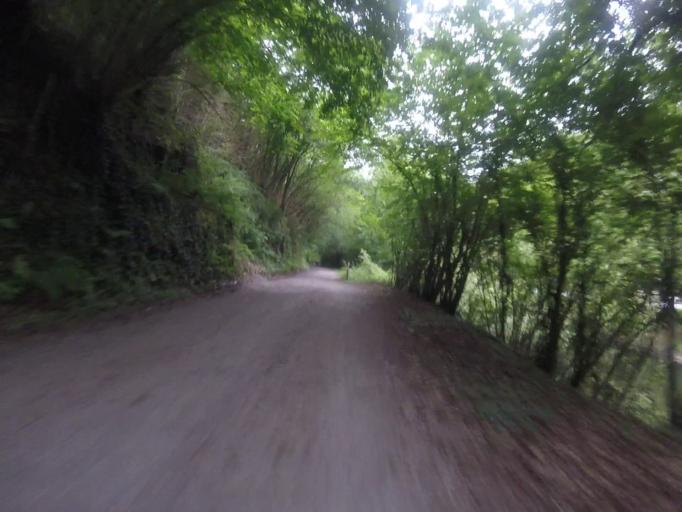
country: ES
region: Navarre
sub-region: Provincia de Navarra
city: Etxalar
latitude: 43.2089
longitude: -1.6651
